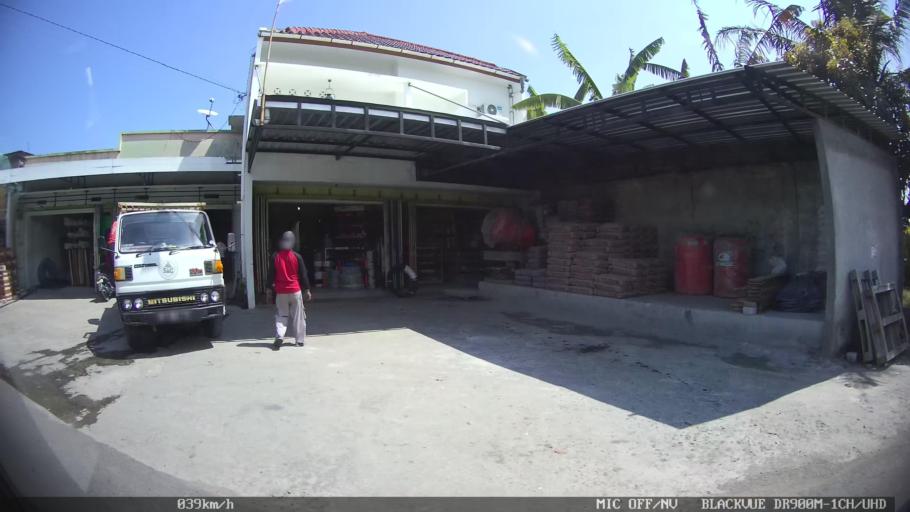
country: ID
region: Daerah Istimewa Yogyakarta
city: Pundong
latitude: -7.9487
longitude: 110.3767
